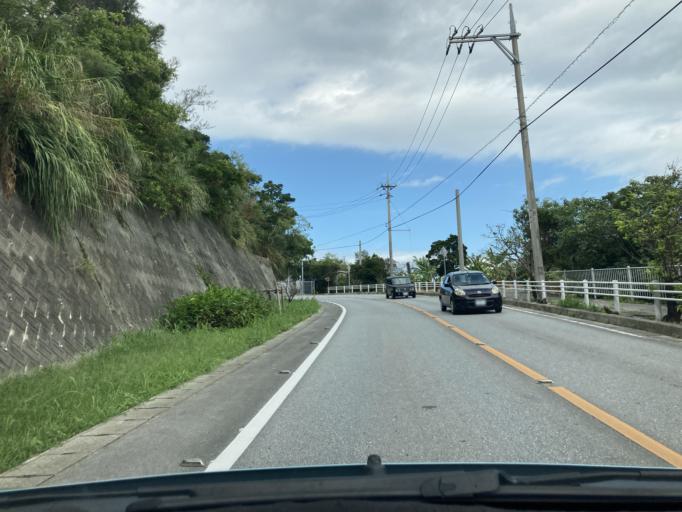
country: JP
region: Okinawa
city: Ginowan
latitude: 26.2675
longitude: 127.7857
